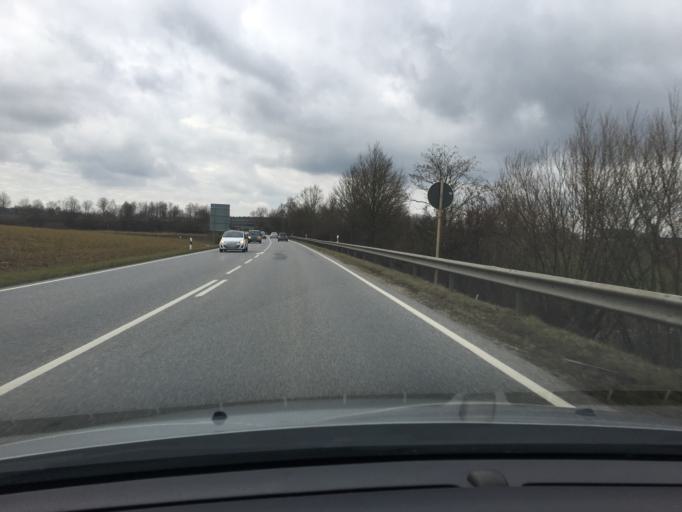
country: DE
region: Bavaria
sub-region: Lower Bavaria
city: Geisenhausen
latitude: 48.4793
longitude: 12.2699
